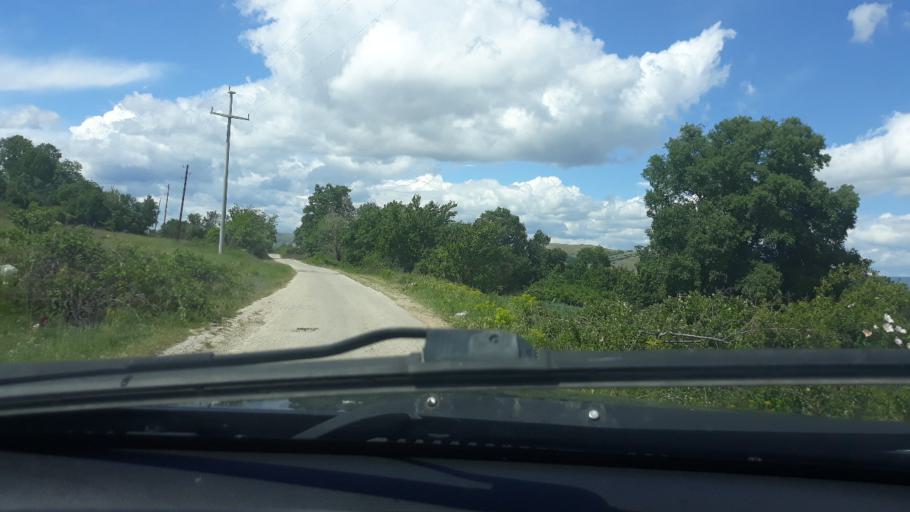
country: MK
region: Krivogastani
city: Krivogashtani
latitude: 41.3259
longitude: 21.3036
